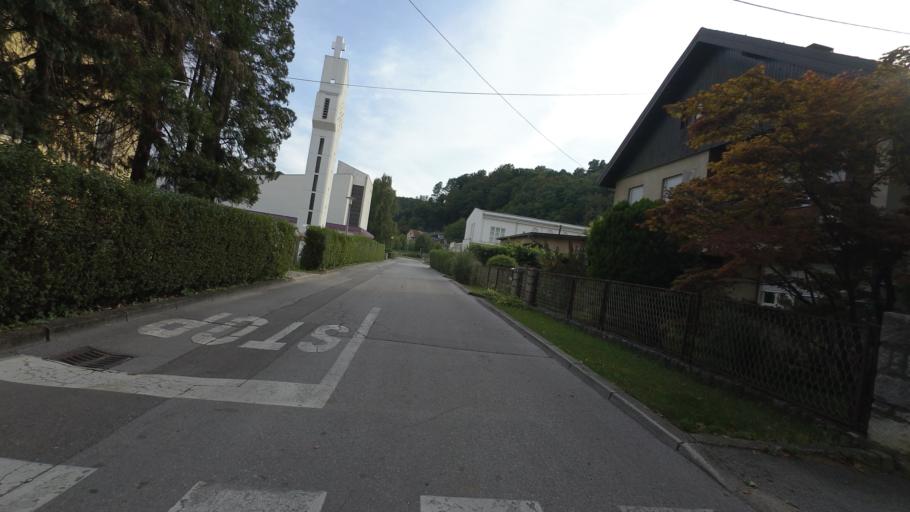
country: HR
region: Karlovacka
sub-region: Grad Karlovac
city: Karlovac
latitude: 45.4961
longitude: 15.5320
